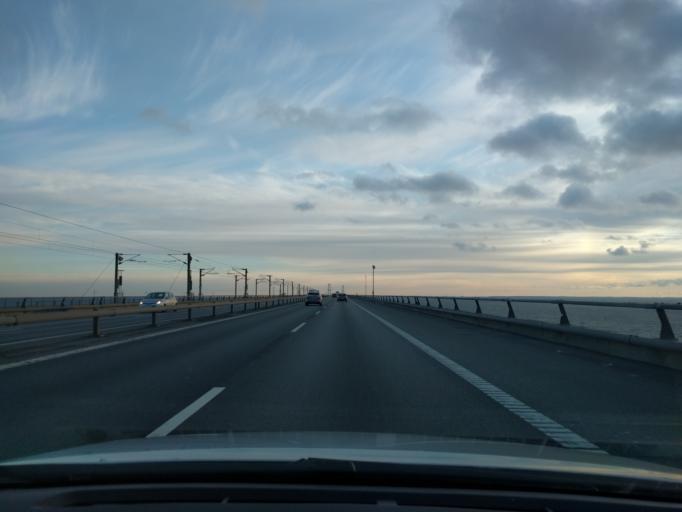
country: DK
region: South Denmark
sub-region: Nyborg Kommune
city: Nyborg
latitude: 55.3055
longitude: 10.8828
